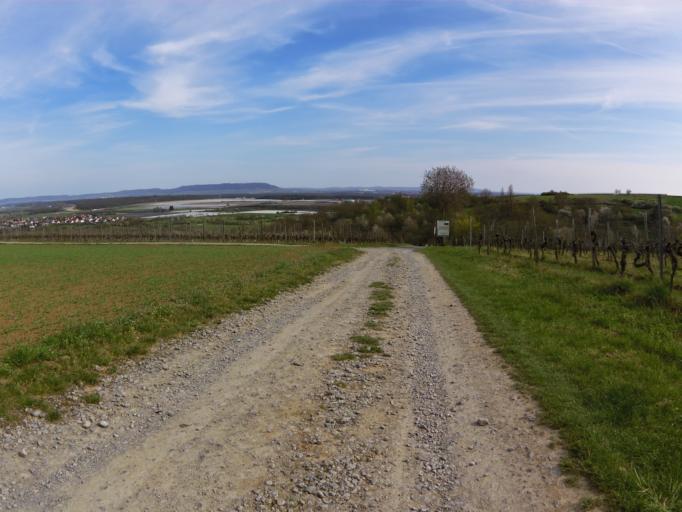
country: DE
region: Bavaria
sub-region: Regierungsbezirk Unterfranken
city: Mainstockheim
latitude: 49.7968
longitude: 10.1472
